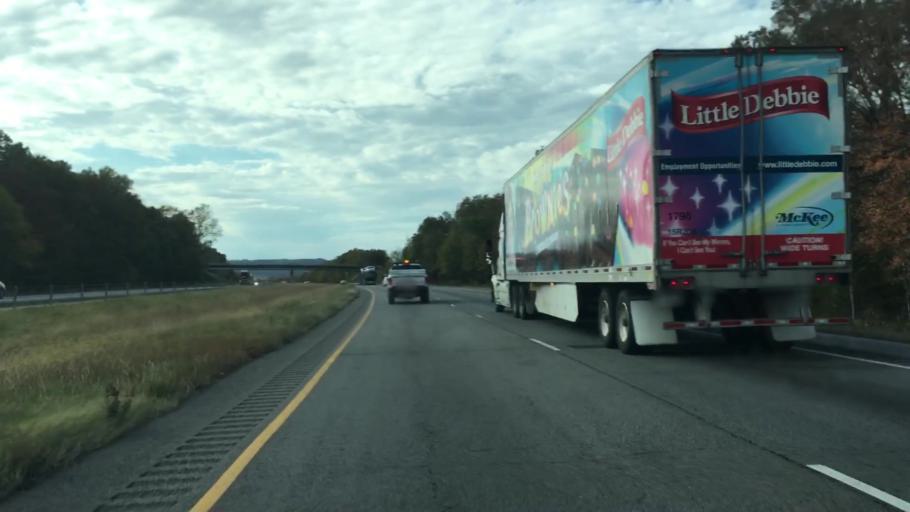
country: US
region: Arkansas
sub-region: Pope County
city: Atkins
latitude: 35.2469
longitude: -92.8688
